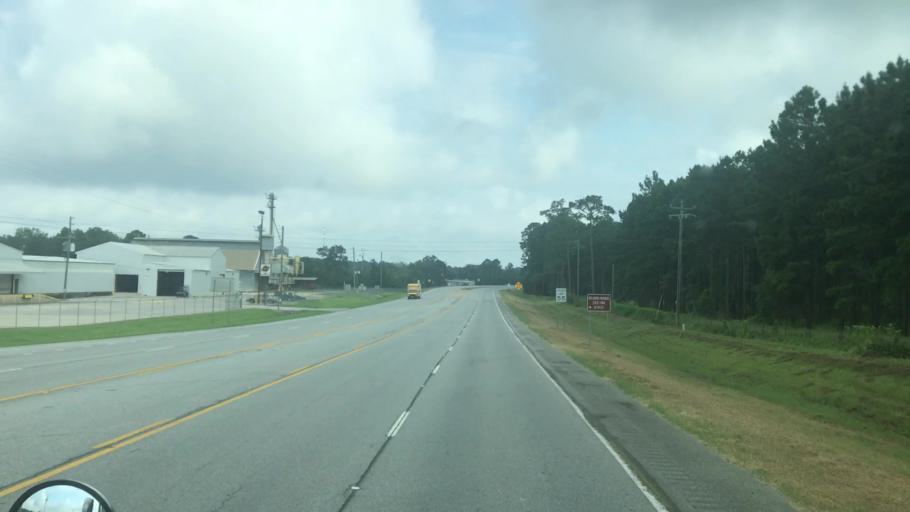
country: US
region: Georgia
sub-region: Miller County
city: Colquitt
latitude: 31.1714
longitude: -84.7564
